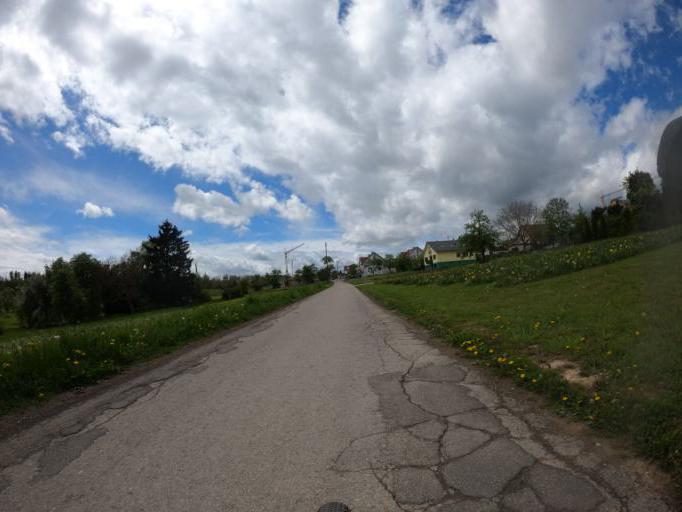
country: DE
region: Baden-Wuerttemberg
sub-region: Regierungsbezirk Stuttgart
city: Oberjettingen
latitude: 48.5734
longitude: 8.7705
